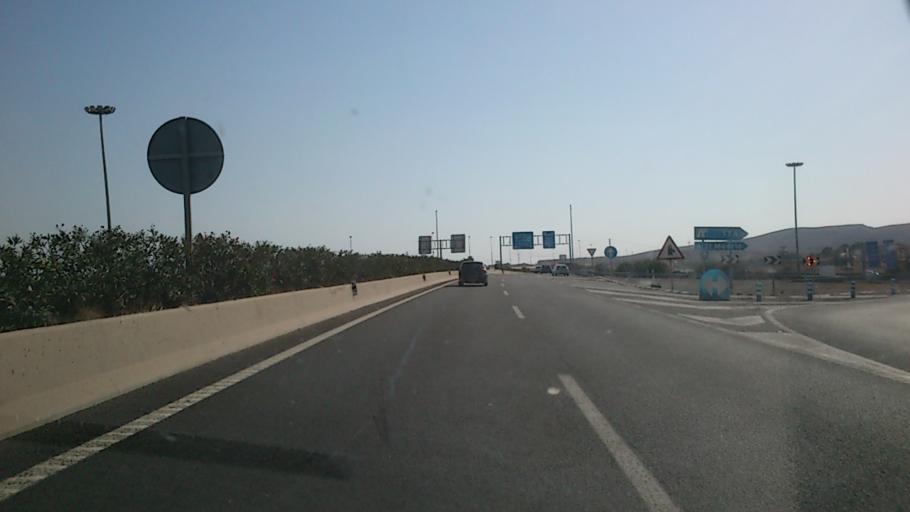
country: ES
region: Valencia
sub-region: Provincia de Alicante
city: San Vicent del Raspeig
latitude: 38.3415
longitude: -0.5433
